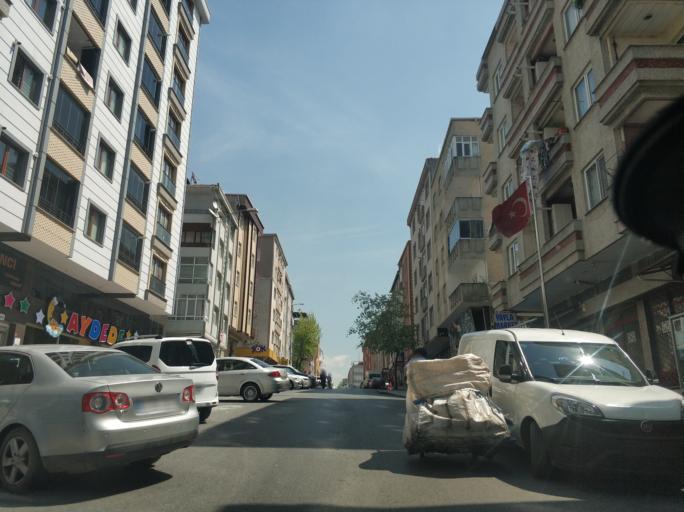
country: TR
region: Istanbul
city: Bagcilar
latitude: 41.0370
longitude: 28.8546
